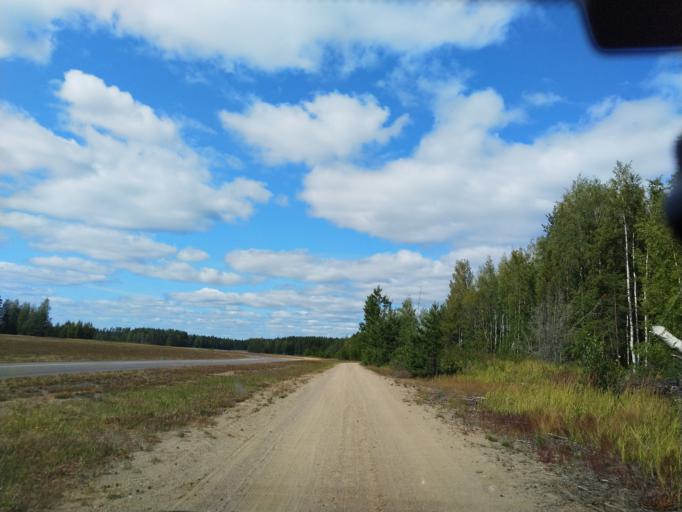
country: FI
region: Uusimaa
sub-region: Helsinki
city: Kaerkoelae
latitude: 60.7504
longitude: 24.1016
